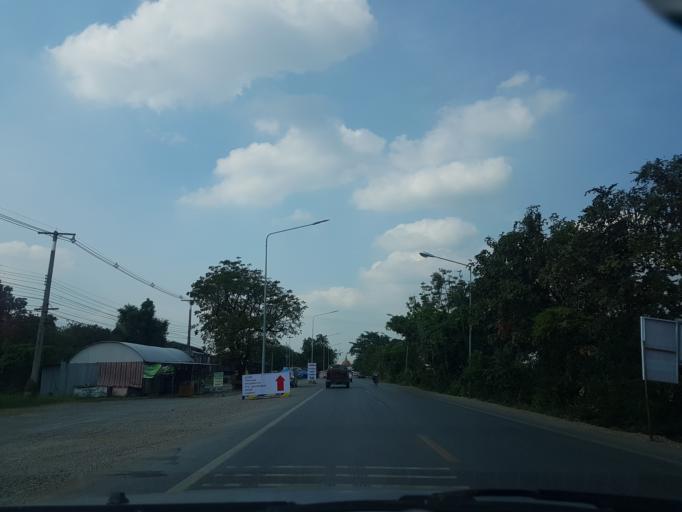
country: TH
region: Phra Nakhon Si Ayutthaya
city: Phachi
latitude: 14.3939
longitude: 100.7953
